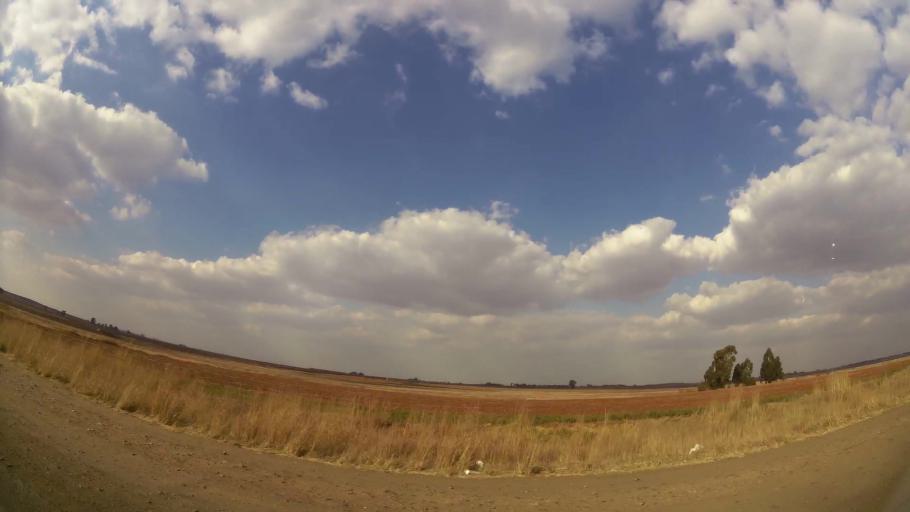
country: ZA
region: Mpumalanga
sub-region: Nkangala District Municipality
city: Delmas
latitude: -26.1583
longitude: 28.6980
